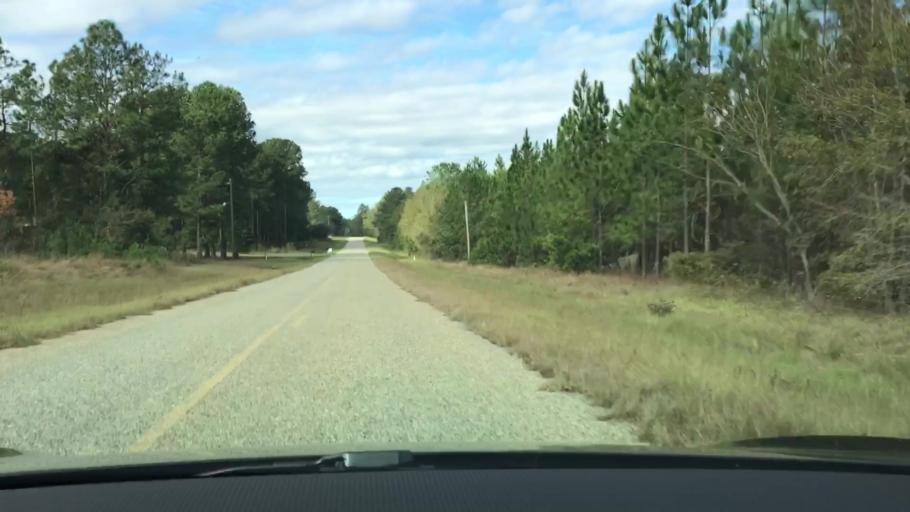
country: US
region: Georgia
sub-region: Jefferson County
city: Wadley
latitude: 32.8096
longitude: -82.3398
